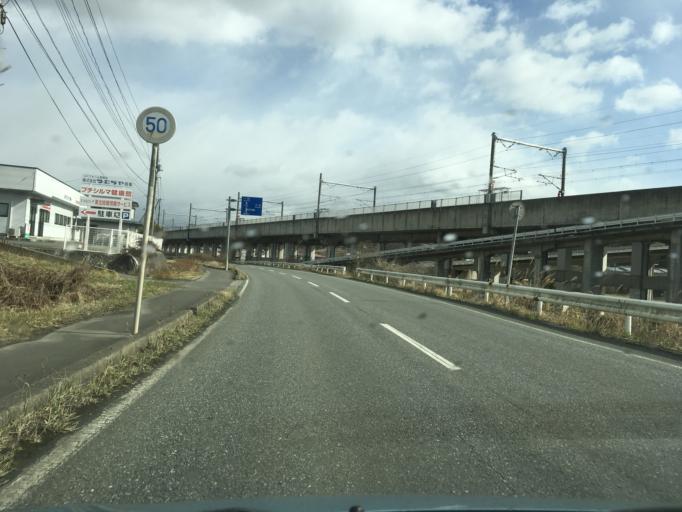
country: JP
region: Iwate
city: Ichinoseki
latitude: 38.8980
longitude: 141.1281
